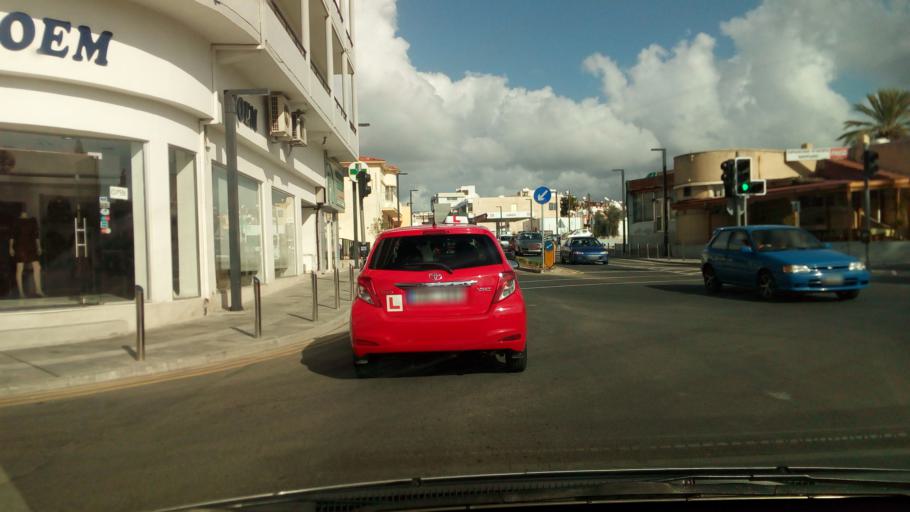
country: CY
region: Pafos
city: Paphos
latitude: 34.7770
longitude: 32.4231
